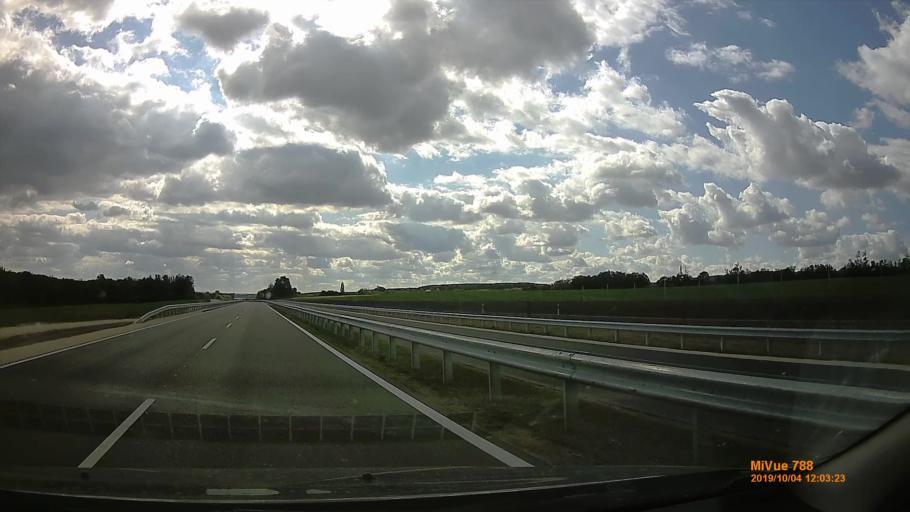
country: HU
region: Somogy
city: Karad
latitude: 46.5881
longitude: 17.8028
